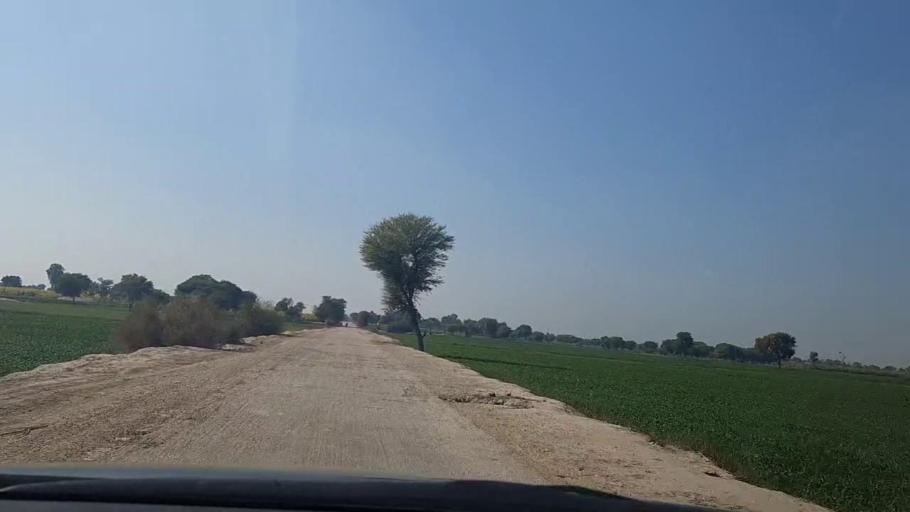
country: PK
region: Sindh
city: Daulatpur
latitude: 26.2846
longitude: 68.0634
